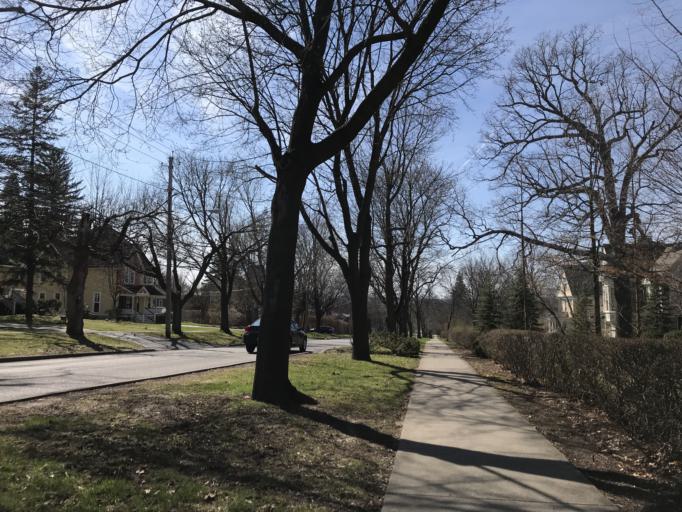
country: US
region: New York
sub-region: Livingston County
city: Geneseo
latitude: 42.7953
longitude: -77.8077
